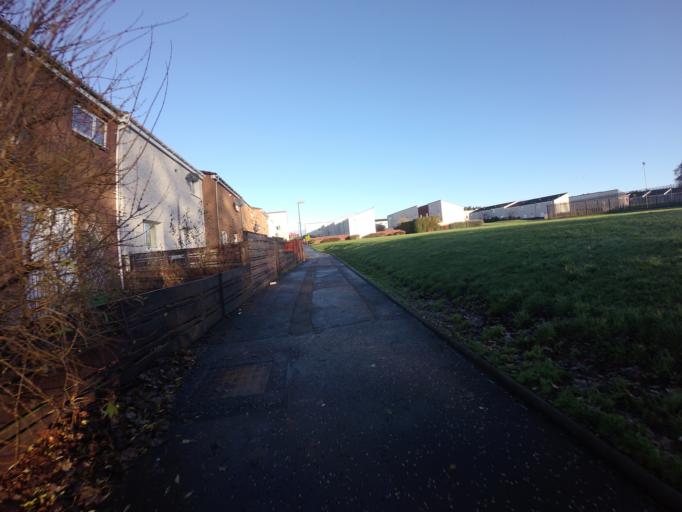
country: GB
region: Scotland
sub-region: West Lothian
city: Livingston
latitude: 55.9089
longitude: -3.5232
